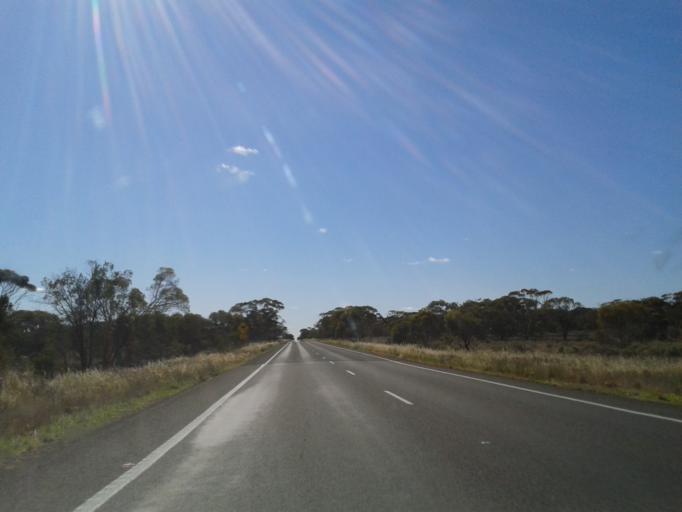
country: AU
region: South Australia
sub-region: Renmark Paringa
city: Renmark
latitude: -34.2743
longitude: 140.9972
